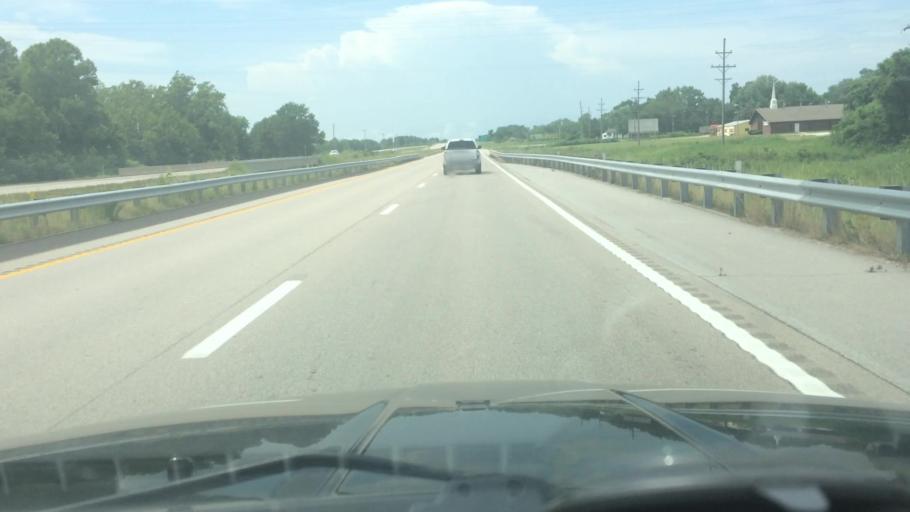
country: US
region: Missouri
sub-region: Polk County
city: Humansville
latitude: 37.7870
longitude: -93.5815
